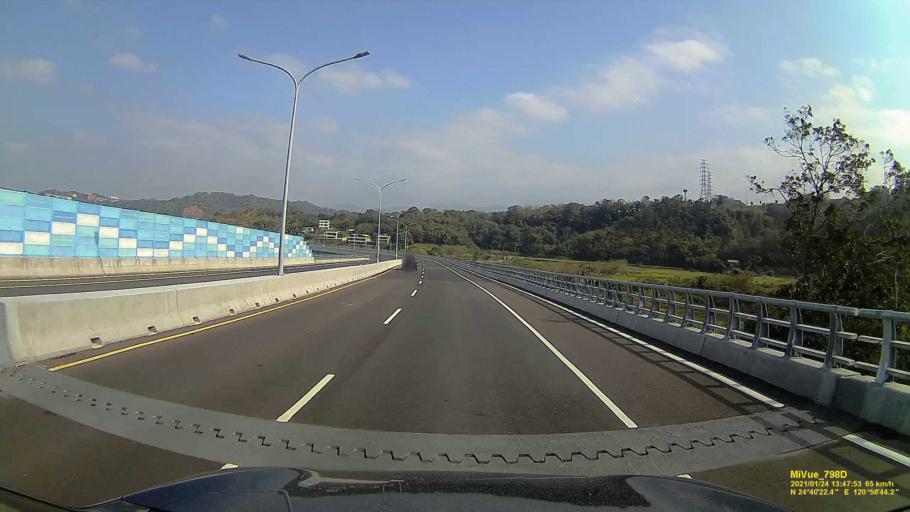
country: TW
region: Taiwan
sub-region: Hsinchu
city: Hsinchu
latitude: 24.6729
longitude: 120.9456
